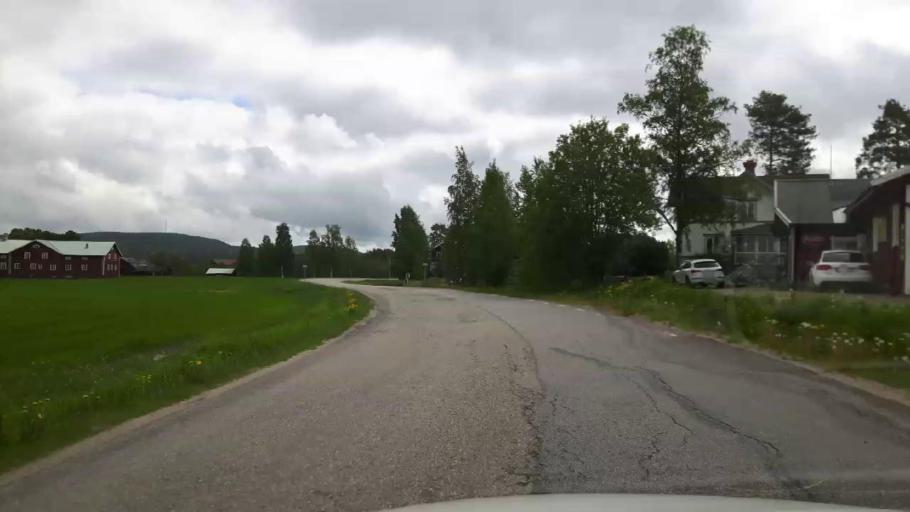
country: SE
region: Gaevleborg
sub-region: Ovanakers Kommun
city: Edsbyn
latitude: 61.3547
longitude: 15.9086
